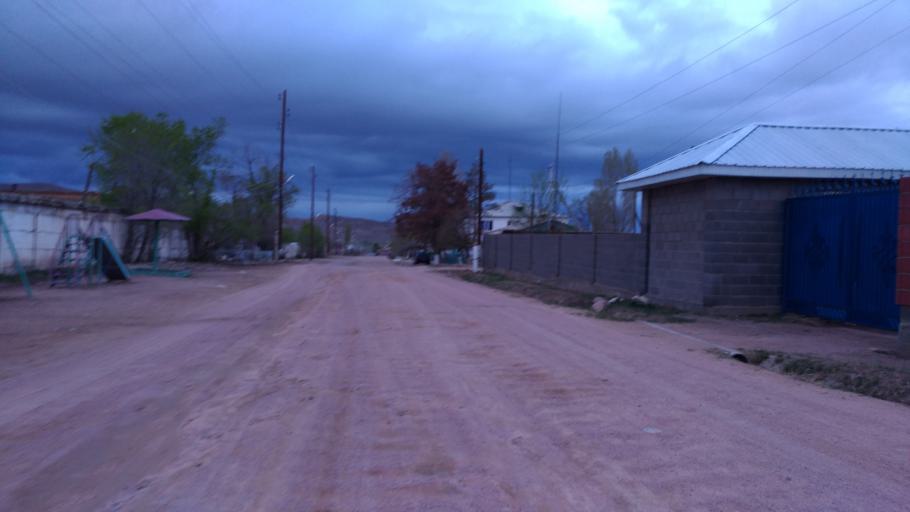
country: KG
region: Ysyk-Koel
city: Bokombayevskoye
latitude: 42.1173
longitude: 76.9879
